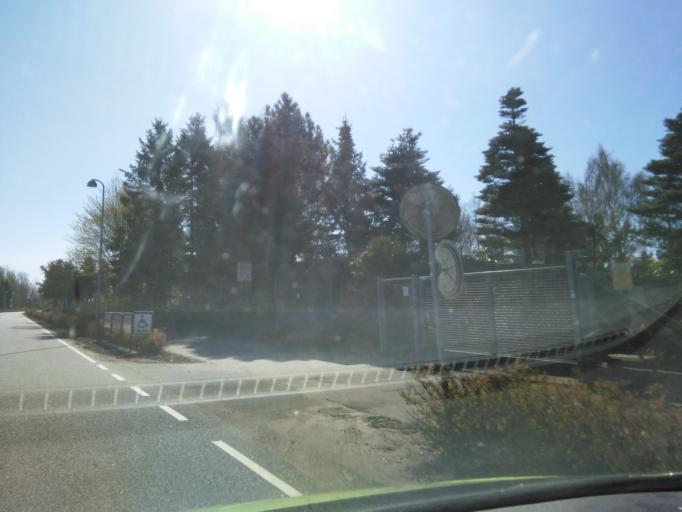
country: DK
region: South Denmark
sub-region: Billund Kommune
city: Billund
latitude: 55.7363
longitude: 9.1283
